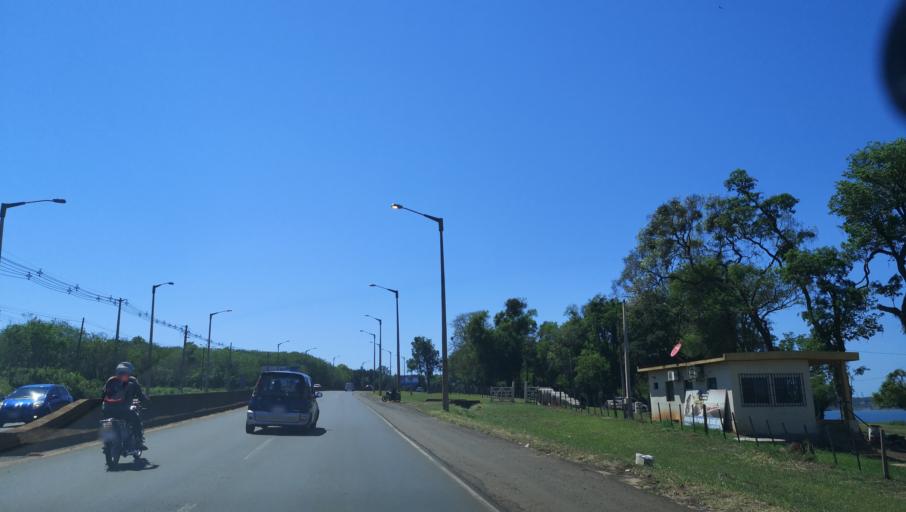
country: PY
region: Itapua
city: San Juan del Parana
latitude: -27.2918
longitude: -55.9181
